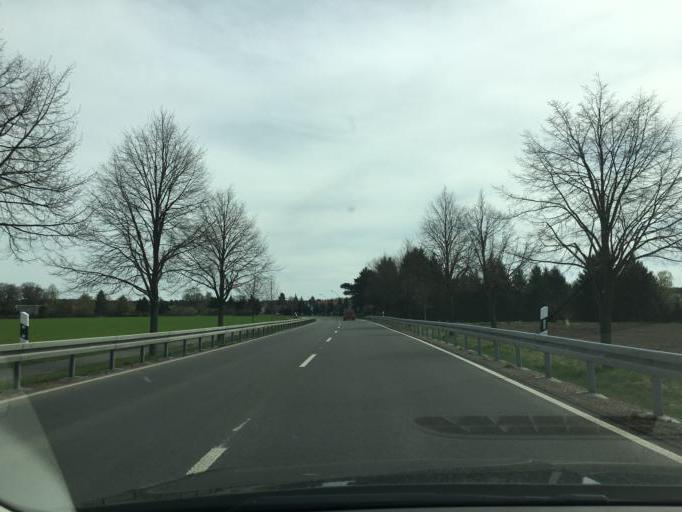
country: DE
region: Saxony
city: Schleife
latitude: 51.5730
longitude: 14.4913
